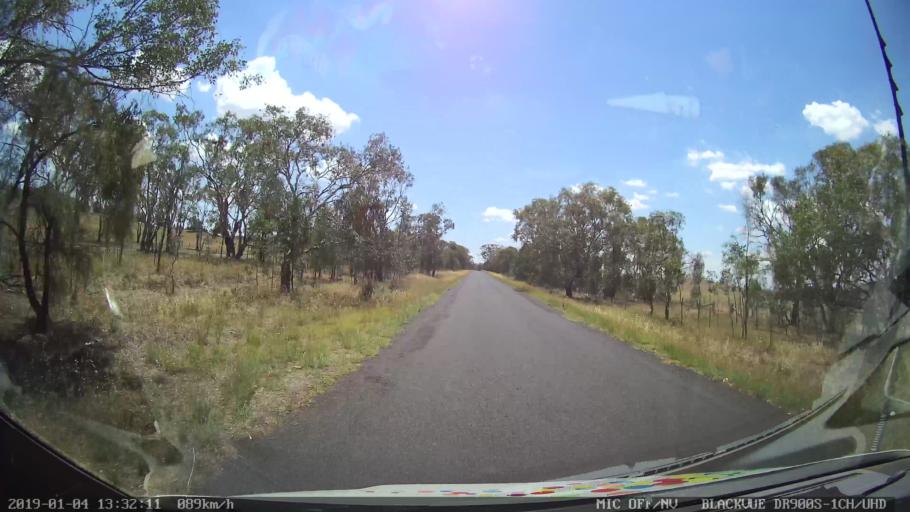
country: AU
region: New South Wales
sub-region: Dubbo Municipality
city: Eulomogo
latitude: -32.6129
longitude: 148.5488
